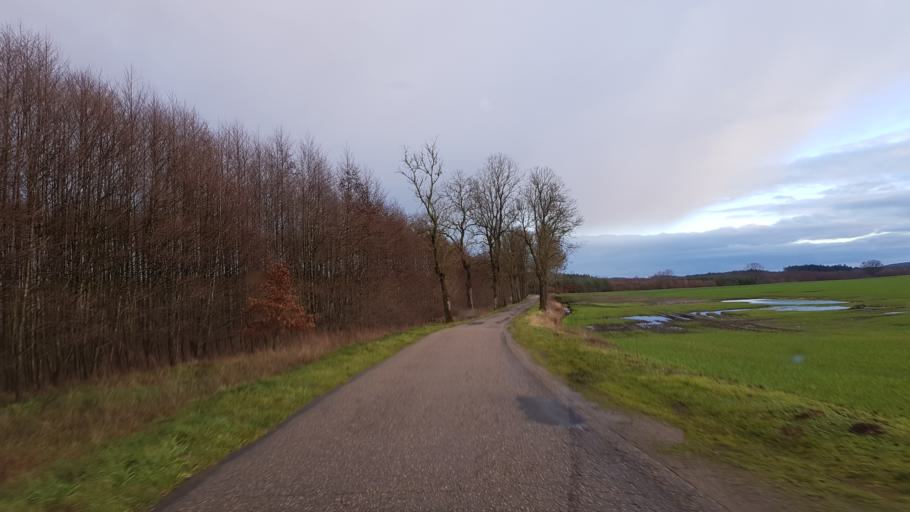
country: PL
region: West Pomeranian Voivodeship
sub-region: Powiat swidwinski
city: Rabino
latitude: 53.9417
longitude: 15.9361
